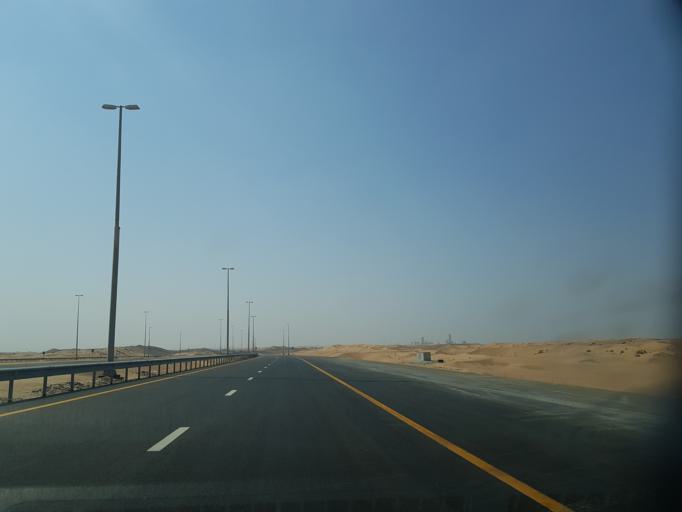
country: AE
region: Ash Shariqah
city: Adh Dhayd
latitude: 25.2676
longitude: 55.6576
